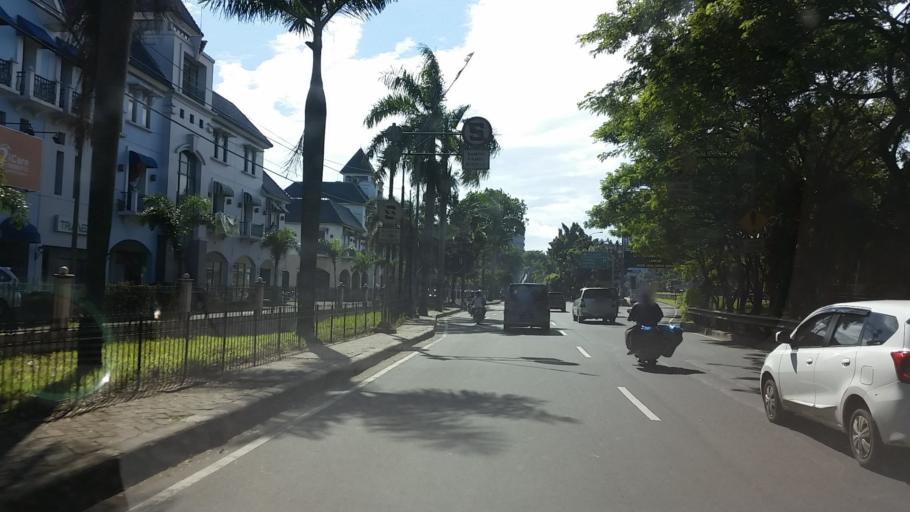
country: ID
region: Banten
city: South Tangerang
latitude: -6.2825
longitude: 106.7734
